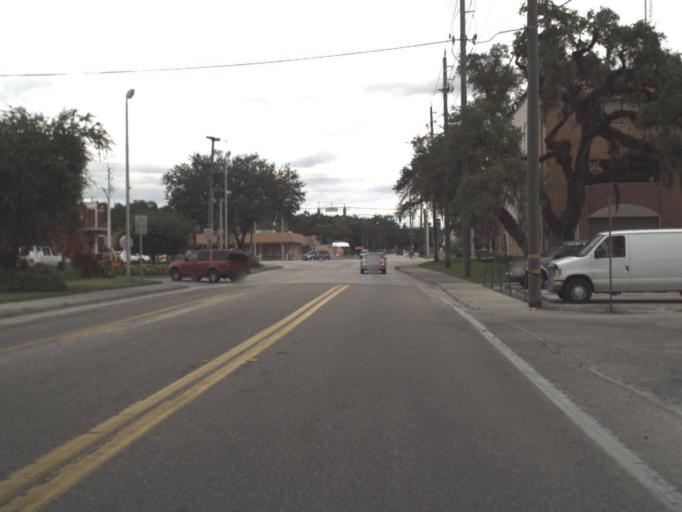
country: US
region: Florida
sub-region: Hendry County
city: LaBelle
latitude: 26.7606
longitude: -81.4384
